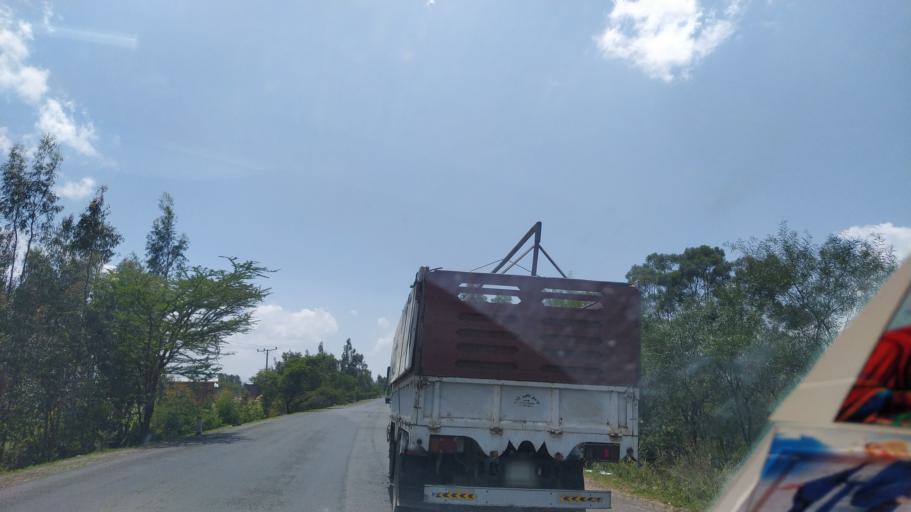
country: ET
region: Southern Nations, Nationalities, and People's Region
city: Butajira
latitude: 7.7818
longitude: 38.1393
